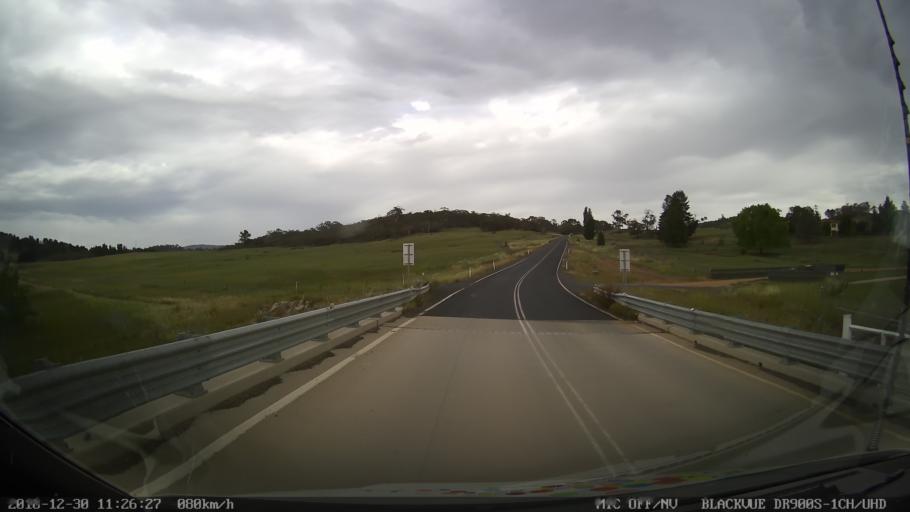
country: AU
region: New South Wales
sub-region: Snowy River
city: Jindabyne
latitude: -36.4684
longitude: 148.6339
